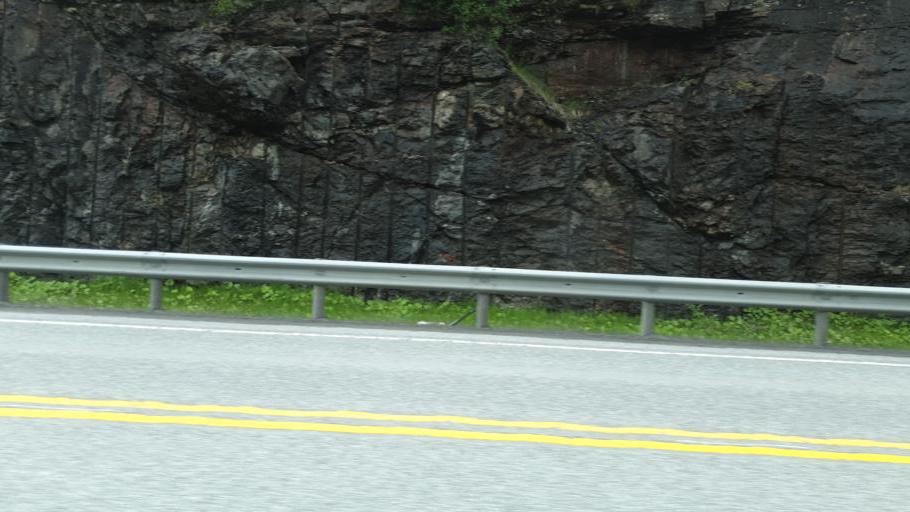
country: NO
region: Sor-Trondelag
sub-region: Midtre Gauldal
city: Storen
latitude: 62.9283
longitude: 10.1685
